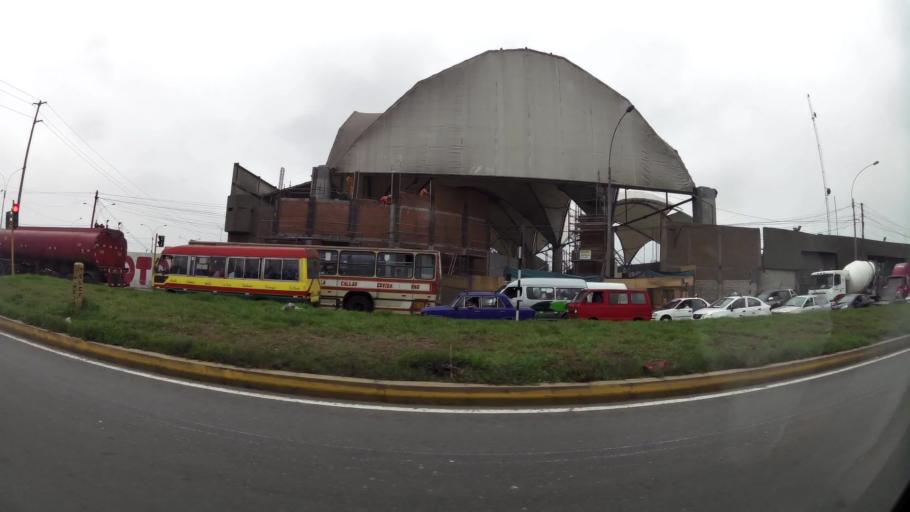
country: PE
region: Callao
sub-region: Callao
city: Callao
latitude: -12.0441
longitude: -77.1265
